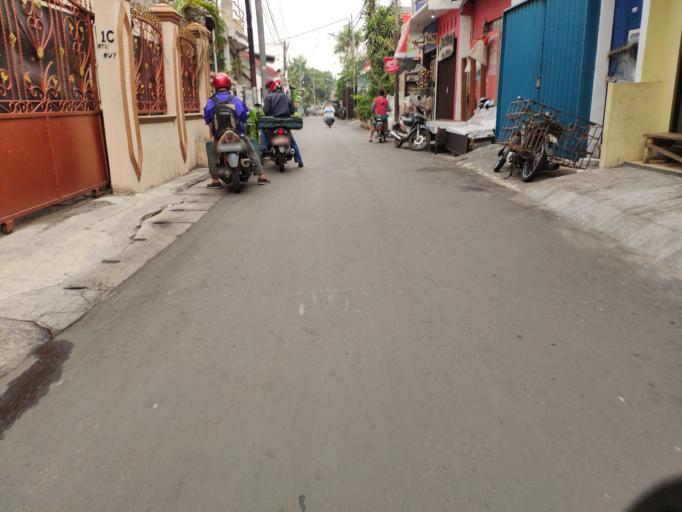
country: ID
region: Jakarta Raya
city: Jakarta
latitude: -6.1970
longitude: 106.8647
